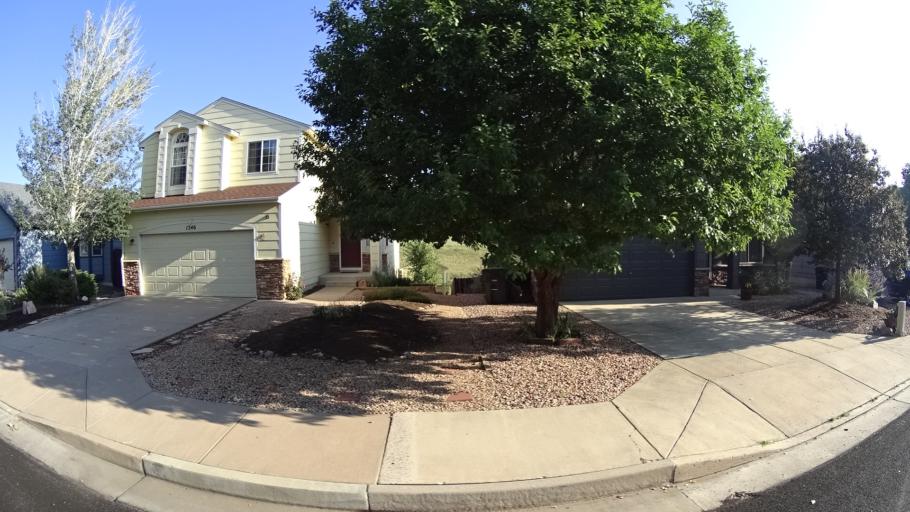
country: US
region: Colorado
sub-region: El Paso County
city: Colorado Springs
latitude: 38.8909
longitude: -104.8524
